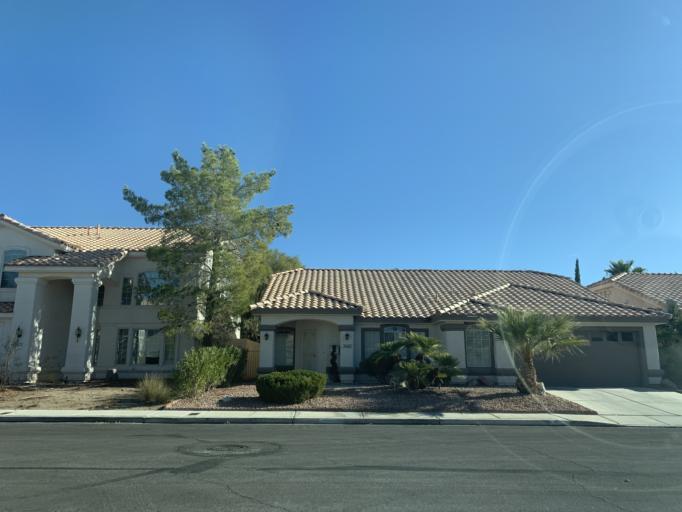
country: US
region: Nevada
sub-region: Clark County
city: Spring Valley
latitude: 36.1227
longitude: -115.2863
